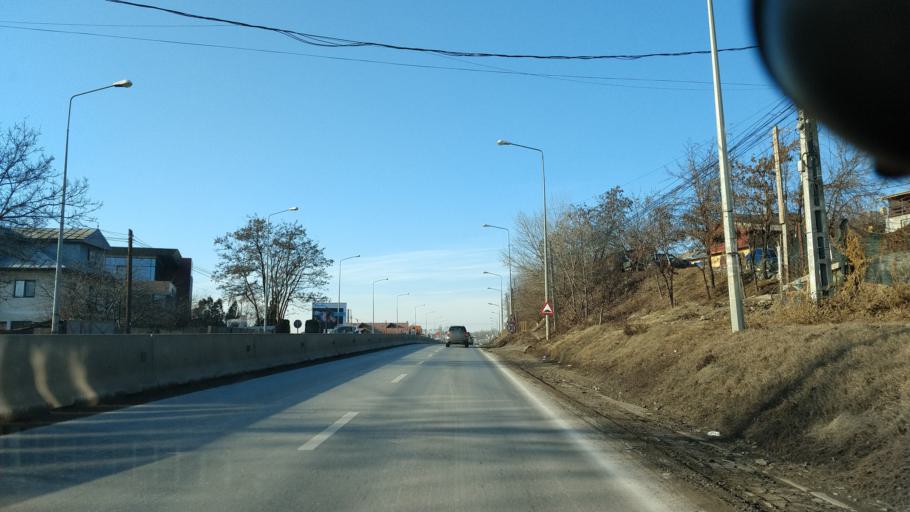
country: RO
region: Iasi
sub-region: Comuna Valea Lupului
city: Valea Lupului
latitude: 47.1736
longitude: 27.5090
